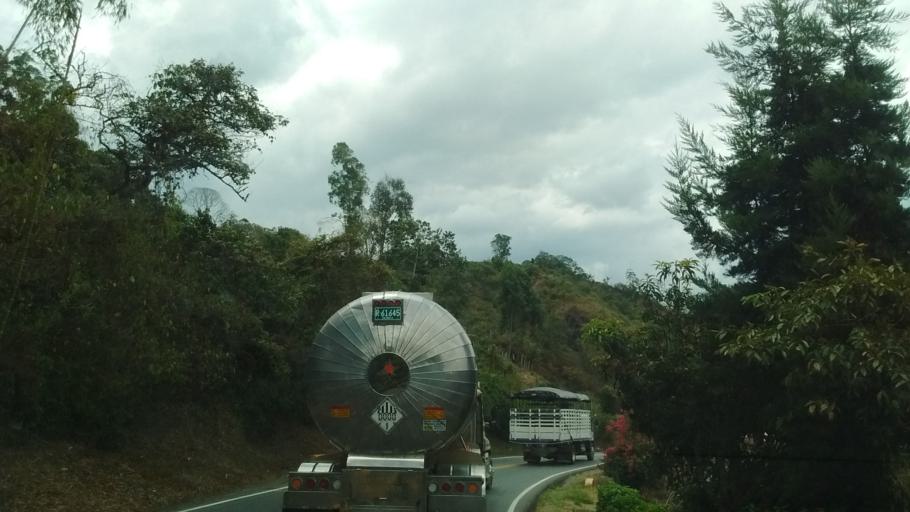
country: CO
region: Cauca
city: Rosas
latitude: 2.3028
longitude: -76.7052
